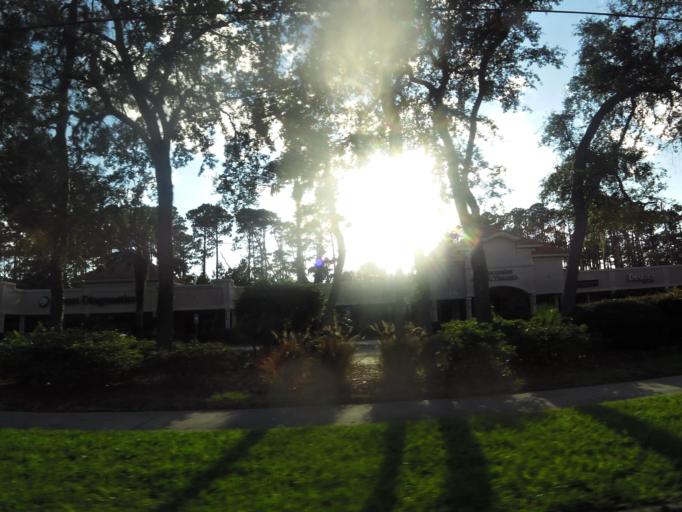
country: US
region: Florida
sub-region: Nassau County
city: Fernandina Beach
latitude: 30.6488
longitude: -81.4548
